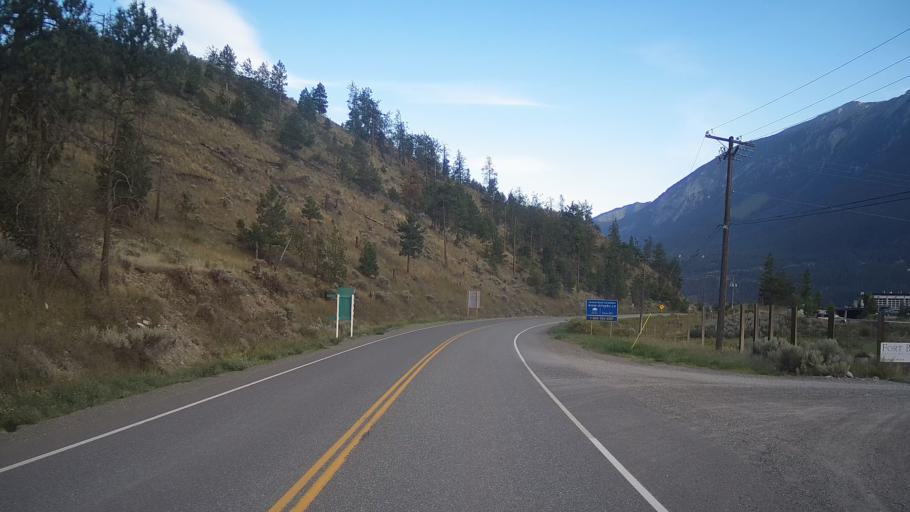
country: CA
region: British Columbia
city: Lillooet
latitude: 50.6902
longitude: -121.9199
